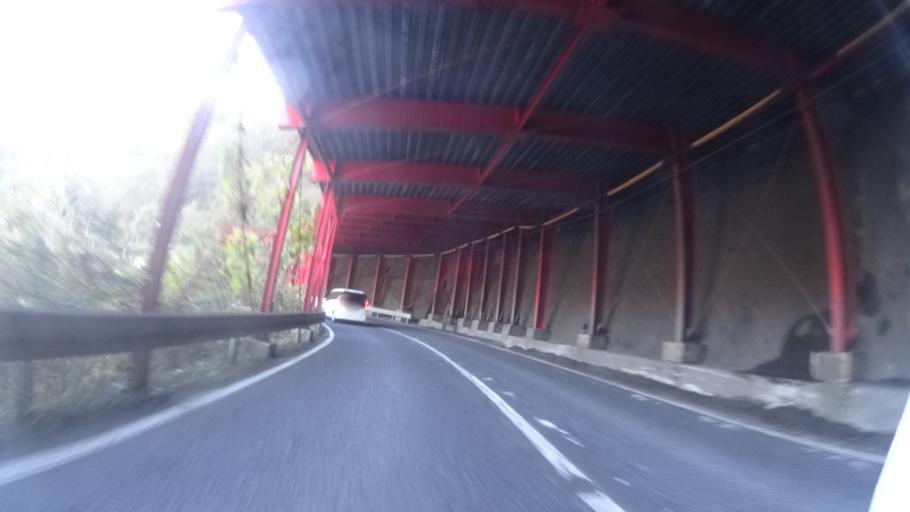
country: JP
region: Fukui
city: Ono
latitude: 35.9652
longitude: 136.5880
